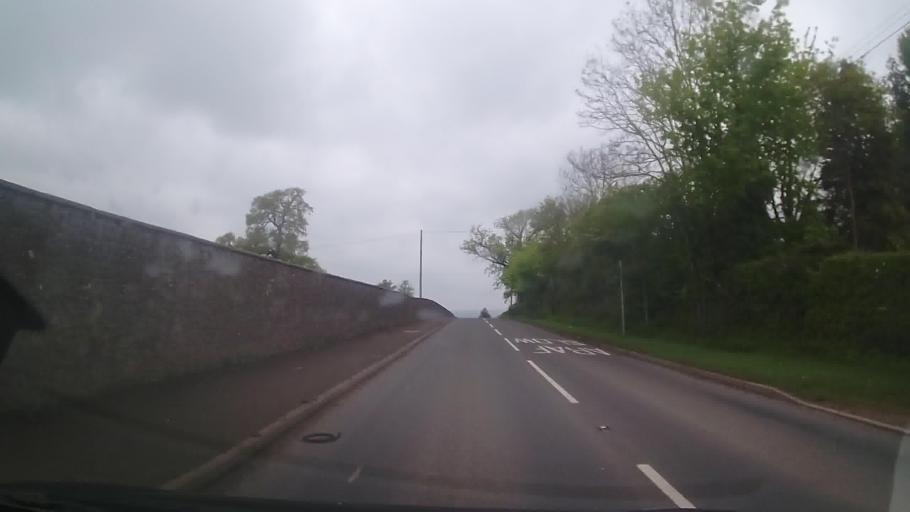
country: GB
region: Wales
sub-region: Wrexham
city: Ruabon
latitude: 52.9819
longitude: -3.0209
